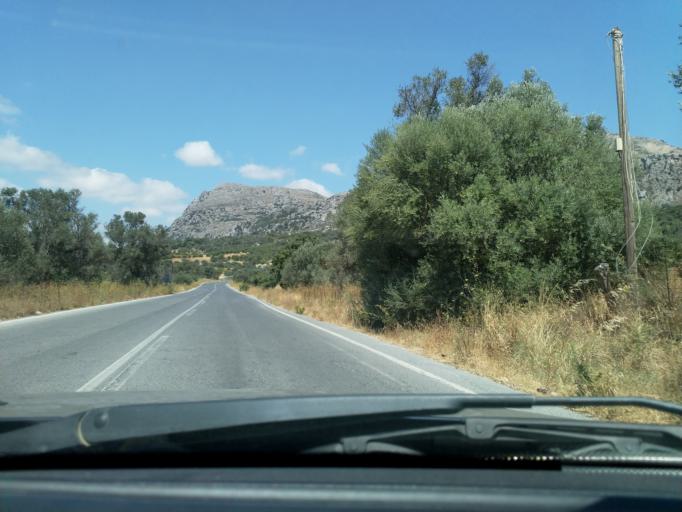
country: GR
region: Crete
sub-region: Nomos Rethymnis
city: Agia Foteini
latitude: 35.1909
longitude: 24.5524
